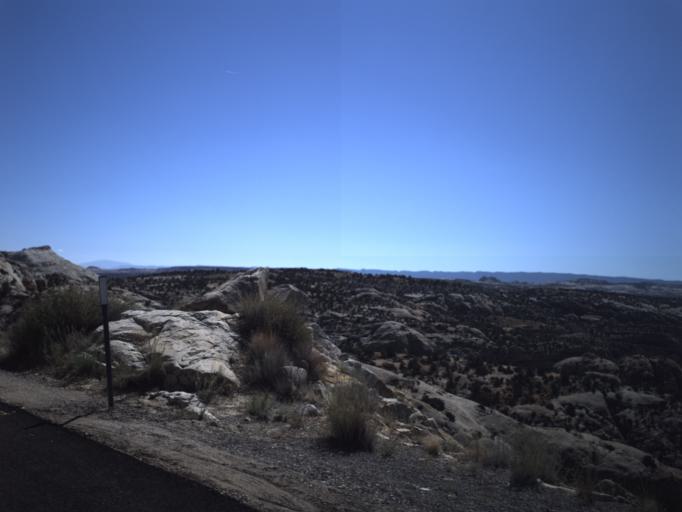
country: US
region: Utah
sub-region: Wayne County
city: Loa
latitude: 37.8126
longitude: -111.4080
